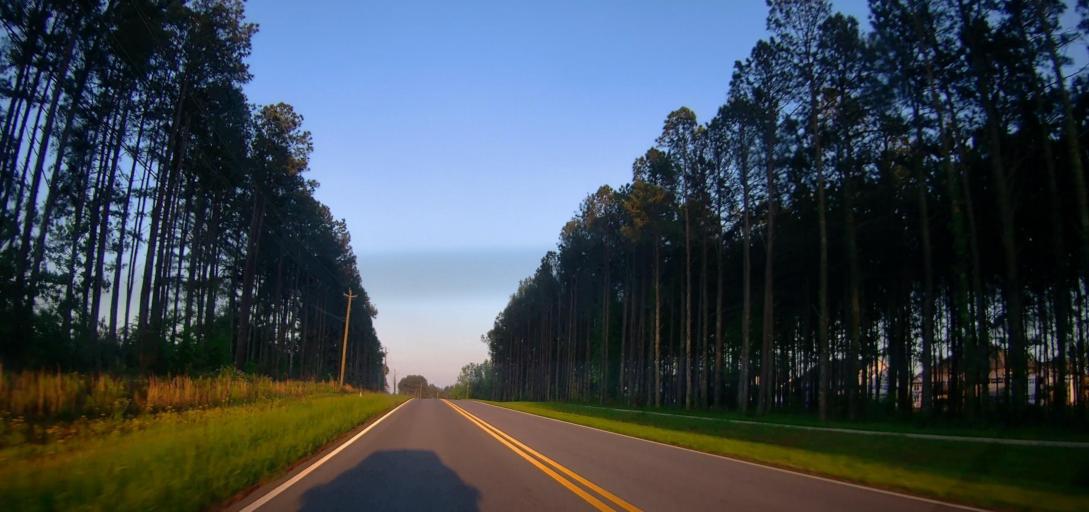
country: US
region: Georgia
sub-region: Henry County
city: McDonough
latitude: 33.4034
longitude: -84.1249
